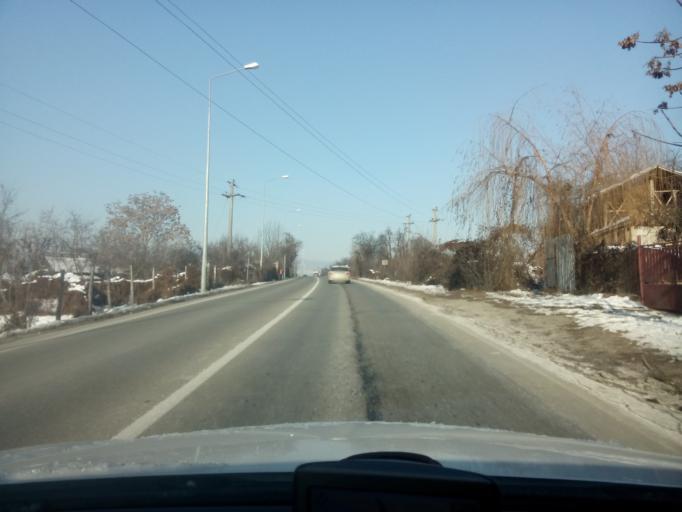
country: RO
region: Valcea
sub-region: Municipiul Ramnicu Valcea
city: Goranu
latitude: 45.1091
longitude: 24.3870
